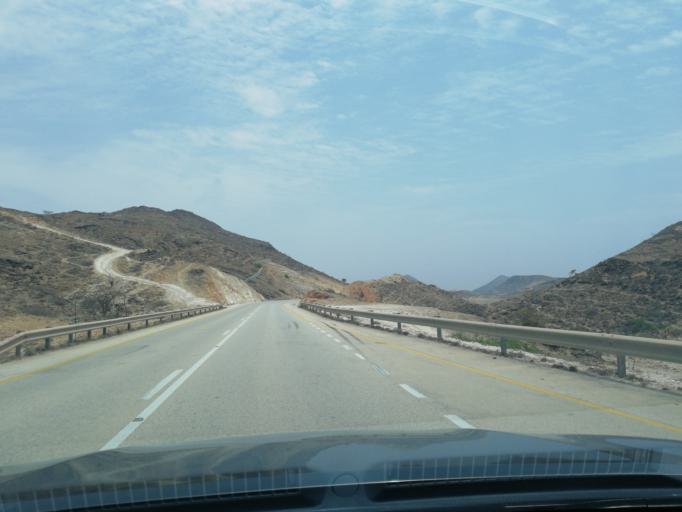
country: OM
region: Zufar
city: Salalah
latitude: 16.8779
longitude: 53.7334
